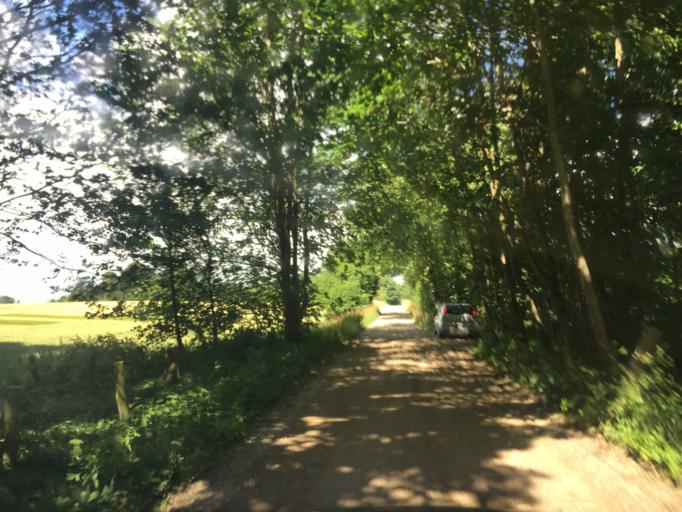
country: DK
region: Capital Region
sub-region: Egedal Kommune
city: Smorumnedre
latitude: 55.7045
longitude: 12.2681
